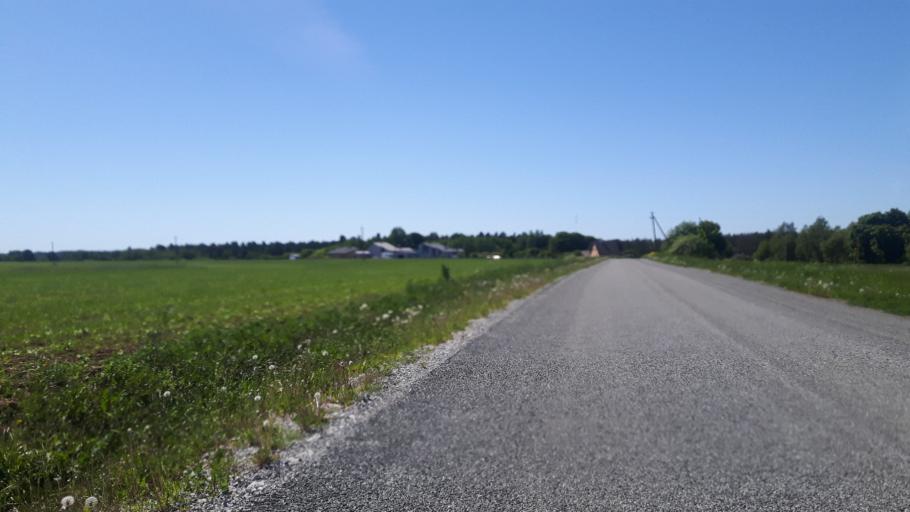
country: EE
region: Ida-Virumaa
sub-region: Toila vald
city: Voka
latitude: 59.4064
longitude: 27.6023
